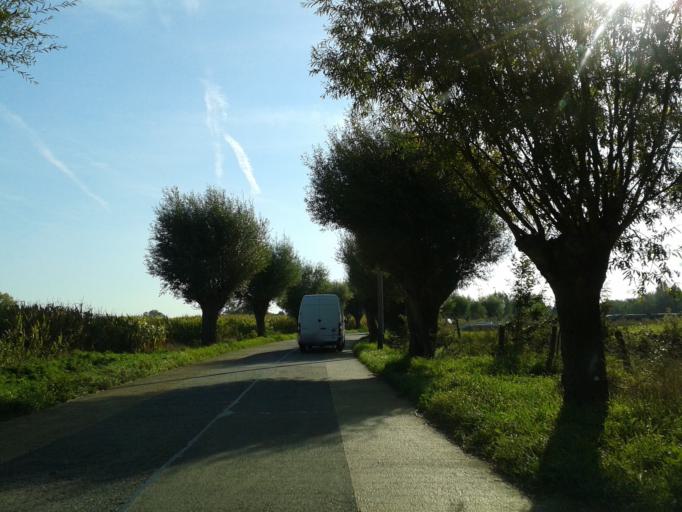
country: BE
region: Flanders
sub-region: Provincie Oost-Vlaanderen
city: Aalst
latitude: 50.9677
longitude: 4.0765
